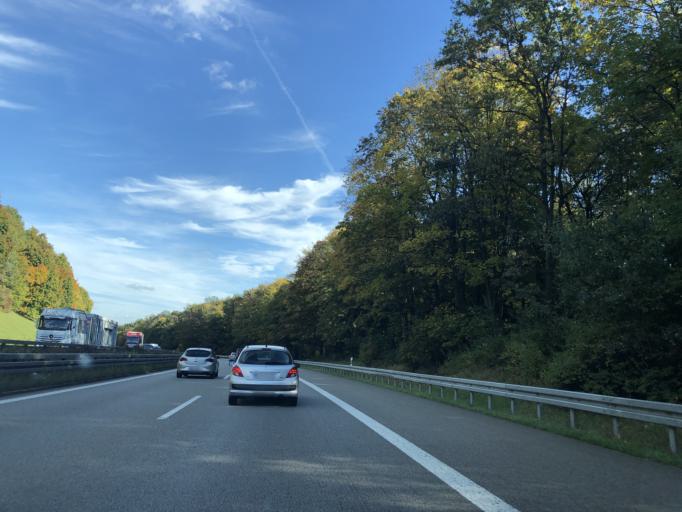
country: DE
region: Bavaria
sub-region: Upper Palatinate
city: Sinzing
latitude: 48.9933
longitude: 12.0105
